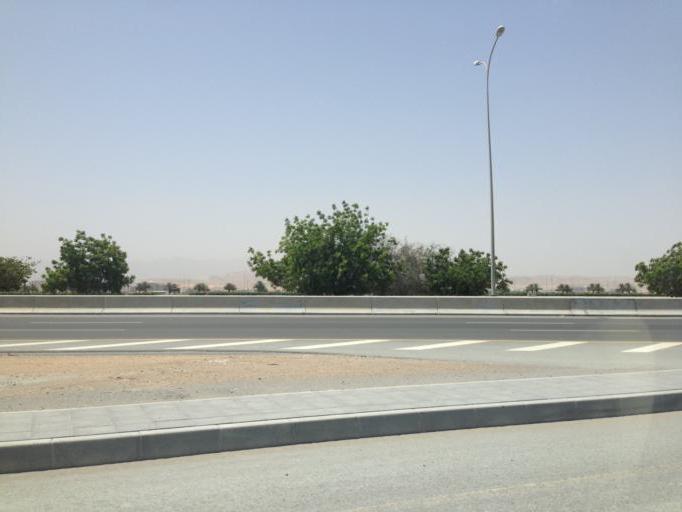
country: OM
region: Muhafazat Masqat
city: Bawshar
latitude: 23.6056
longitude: 58.3240
